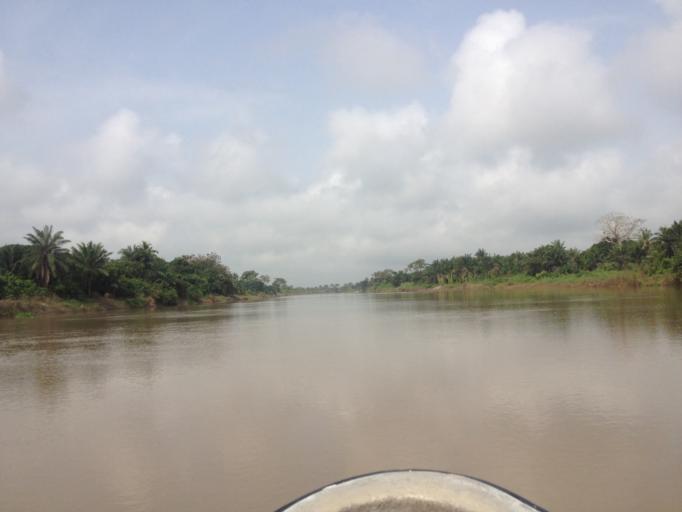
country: BJ
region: Mono
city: Come
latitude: 6.3837
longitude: 1.7839
